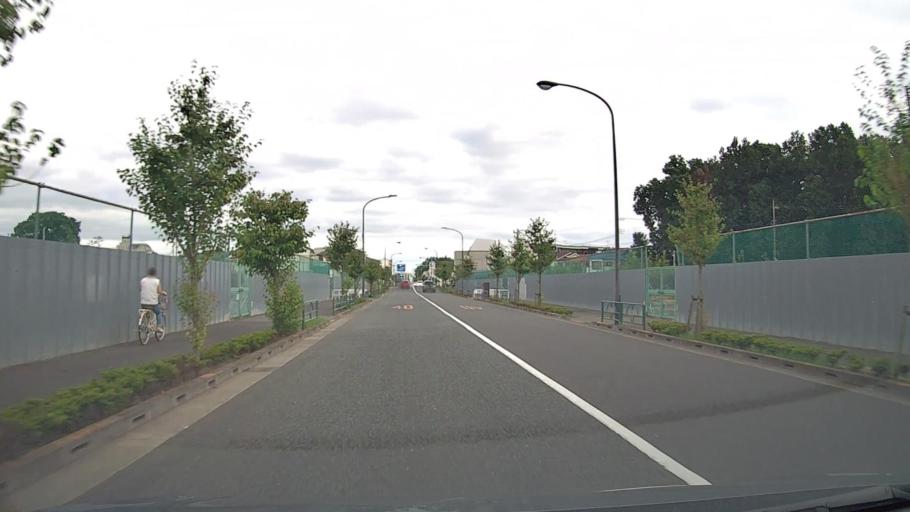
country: JP
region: Tokyo
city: Tanashicho
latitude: 35.7435
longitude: 139.5209
